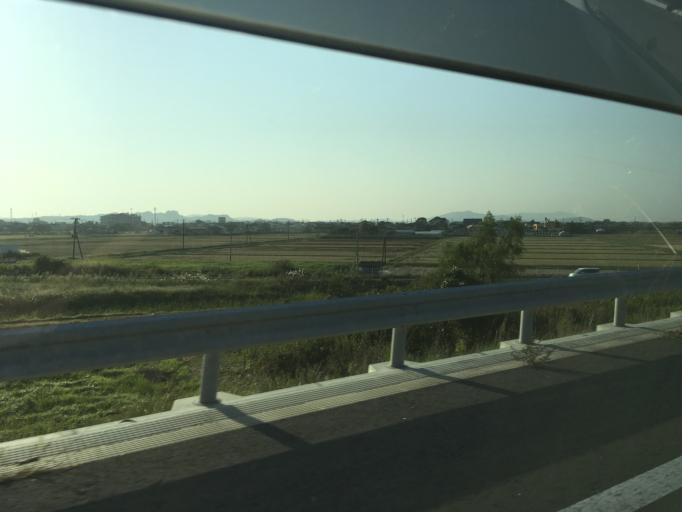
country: JP
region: Miyagi
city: Ishinomaki
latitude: 38.4852
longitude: 141.2919
